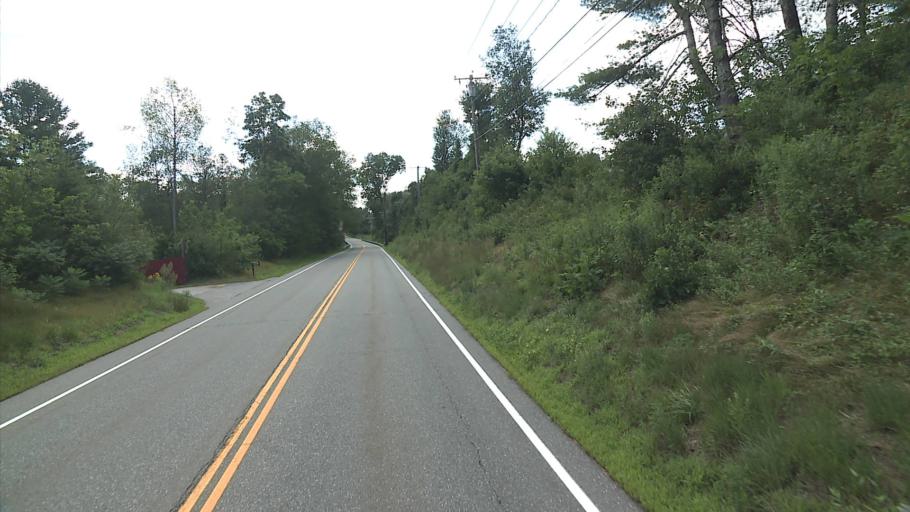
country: US
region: Connecticut
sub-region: Tolland County
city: Storrs
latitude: 41.8476
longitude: -72.0965
